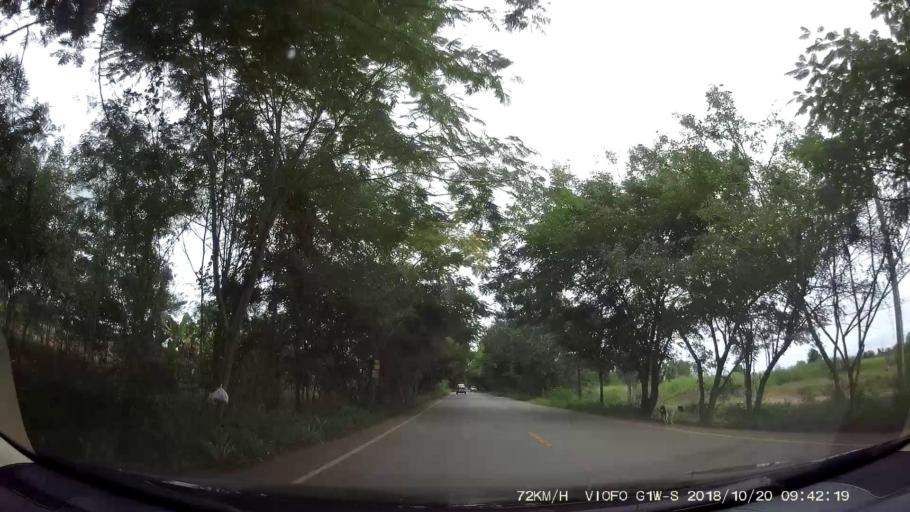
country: TH
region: Chaiyaphum
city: Khon San
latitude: 16.4626
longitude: 101.9529
